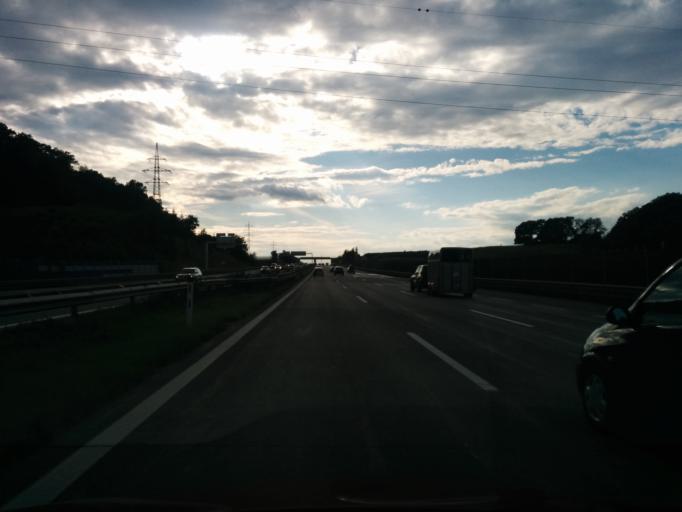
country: AT
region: Lower Austria
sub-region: Sankt Polten Stadt
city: Sankt Poelten
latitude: 48.1773
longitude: 15.6082
